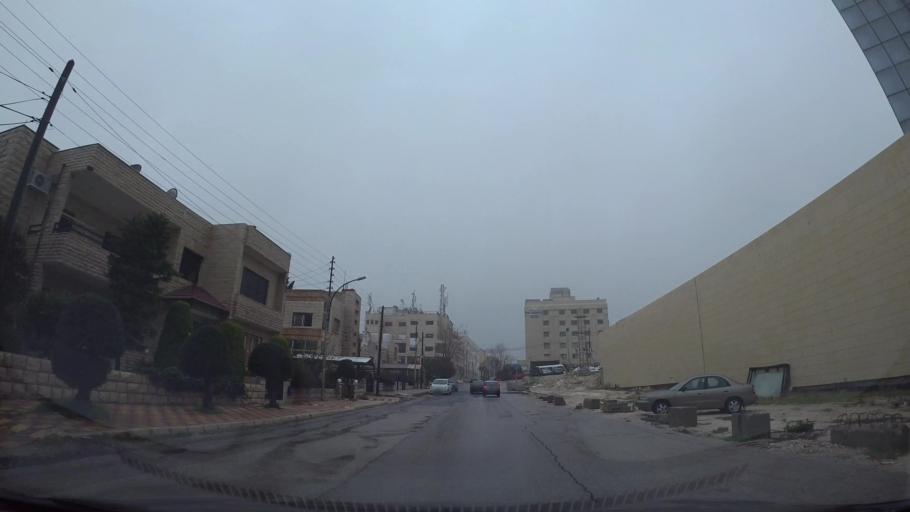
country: JO
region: Amman
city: Wadi as Sir
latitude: 31.9630
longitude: 35.8683
